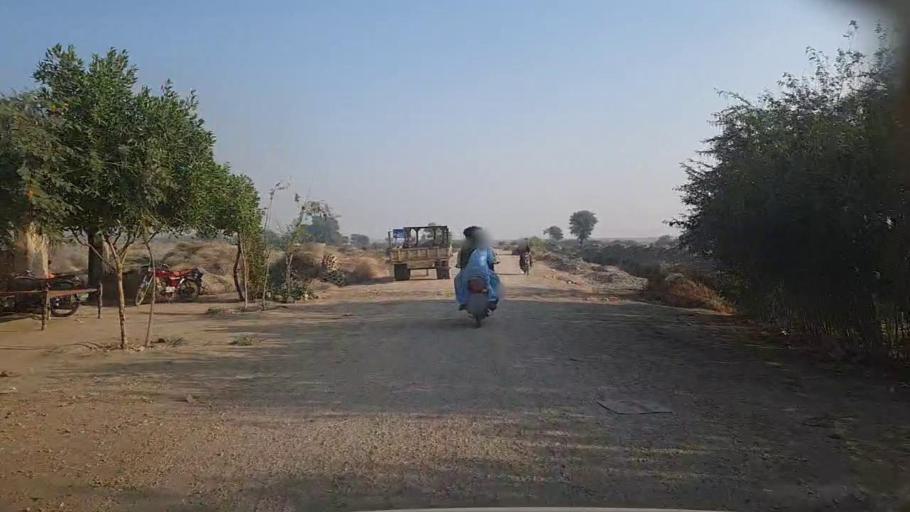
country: PK
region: Sindh
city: Karaundi
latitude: 26.7220
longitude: 68.4920
